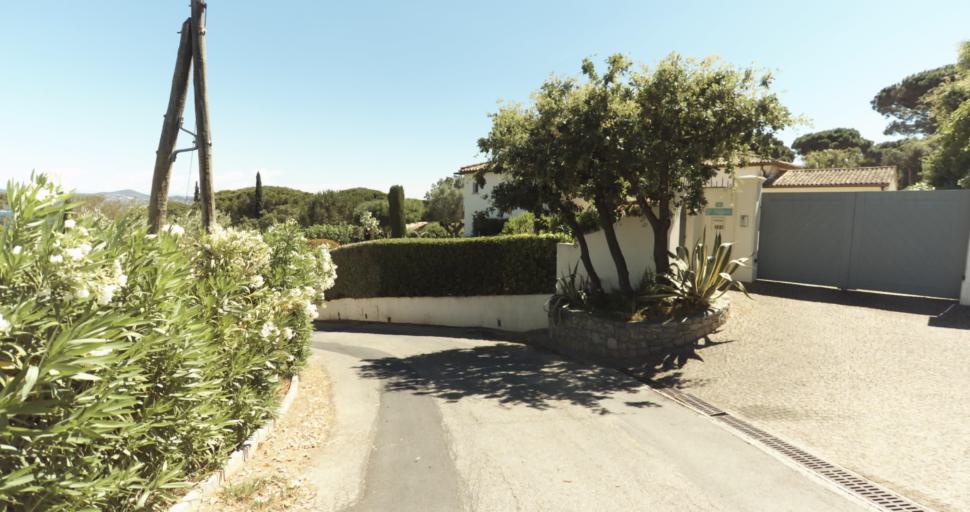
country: FR
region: Provence-Alpes-Cote d'Azur
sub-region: Departement du Var
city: Saint-Tropez
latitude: 43.2615
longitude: 6.6052
